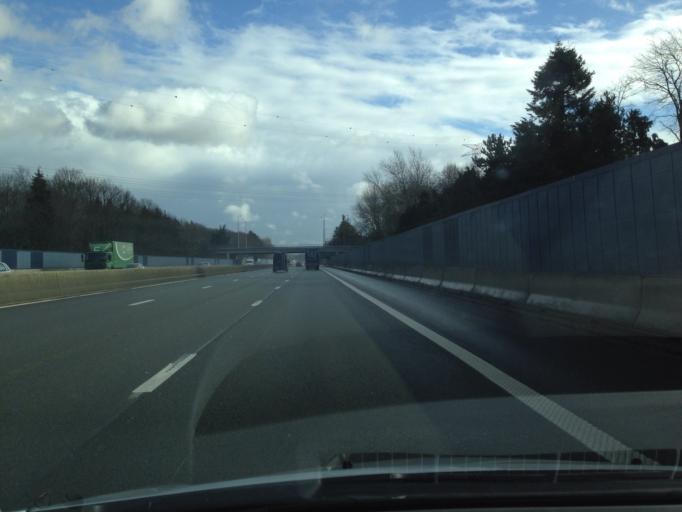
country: BE
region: Flanders
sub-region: Provincie West-Vlaanderen
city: Zedelgem
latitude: 51.1786
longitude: 3.1293
